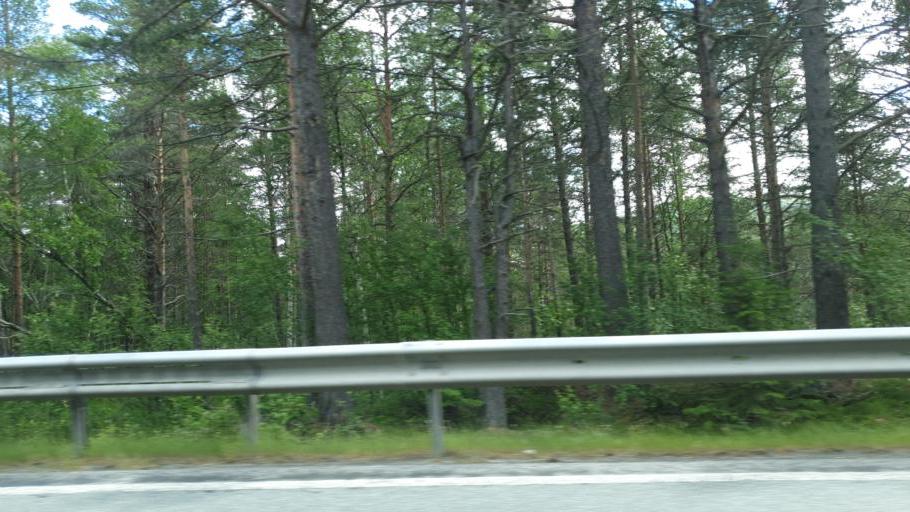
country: NO
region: Sor-Trondelag
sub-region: Rennebu
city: Berkak
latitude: 62.6875
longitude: 9.9314
